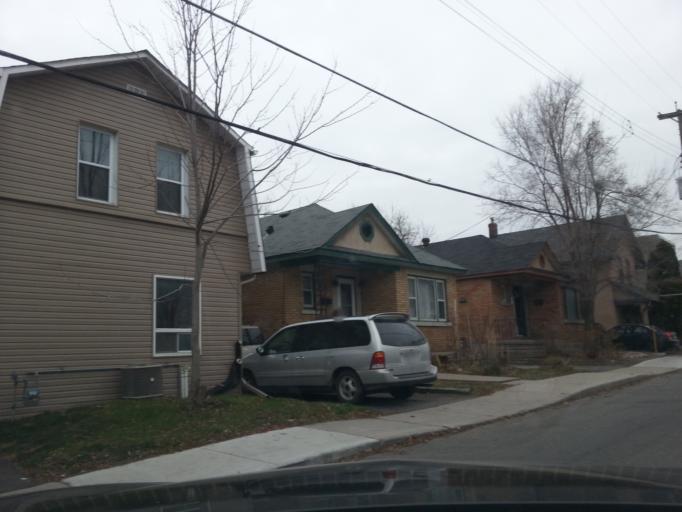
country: CA
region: Ontario
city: Ottawa
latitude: 45.4384
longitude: -75.6562
